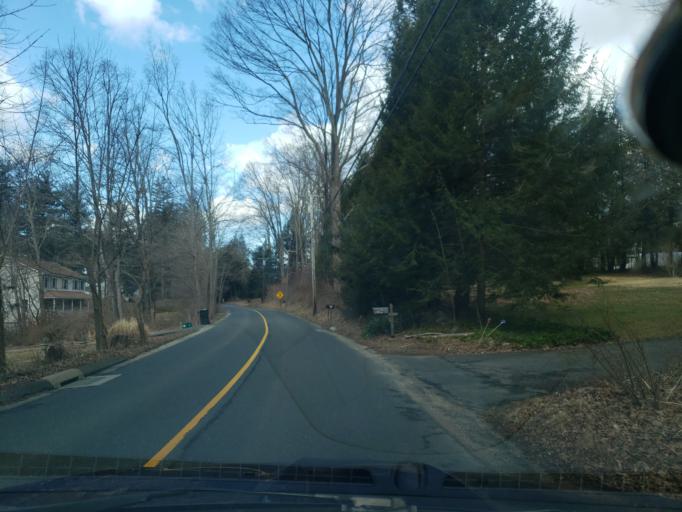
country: US
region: Connecticut
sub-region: Fairfield County
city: Bethel
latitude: 41.3884
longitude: -73.3798
